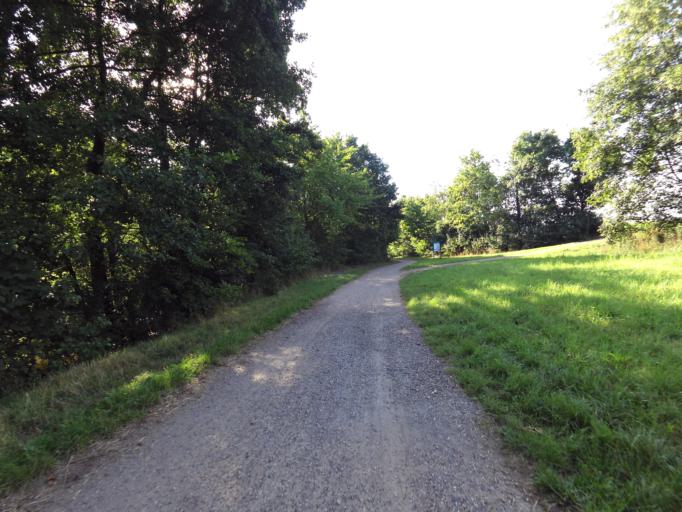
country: DE
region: North Rhine-Westphalia
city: Huckelhoven
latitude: 51.0369
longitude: 6.2271
